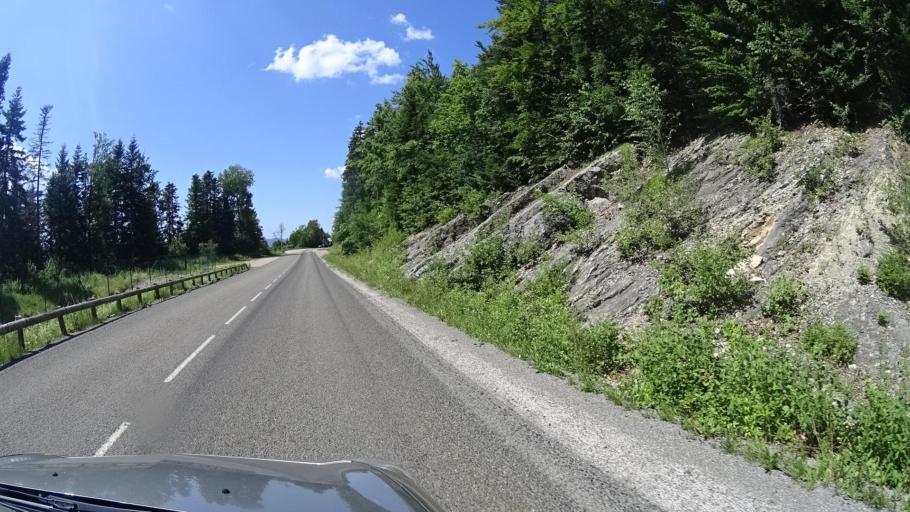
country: FR
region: Franche-Comte
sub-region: Departement du Jura
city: Longchaumois
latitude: 46.4976
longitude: 5.9265
